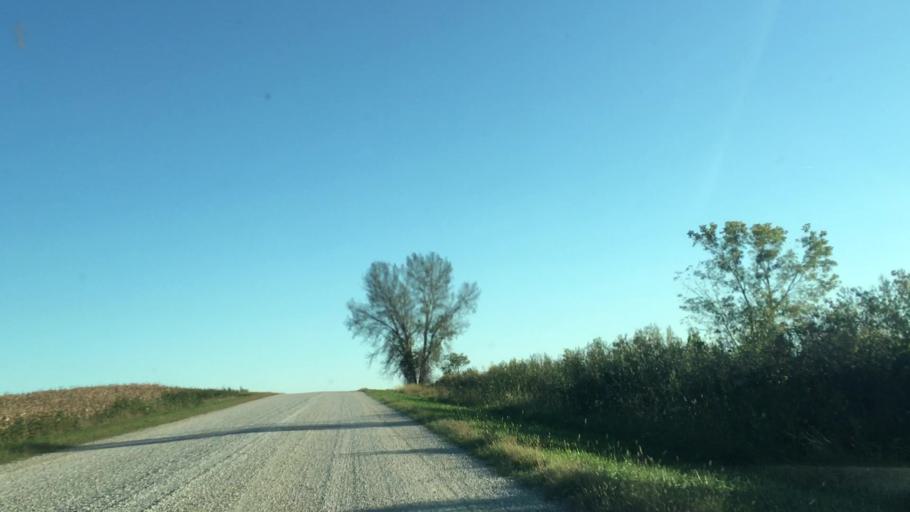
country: US
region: Minnesota
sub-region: Fillmore County
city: Preston
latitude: 43.8037
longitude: -92.0395
